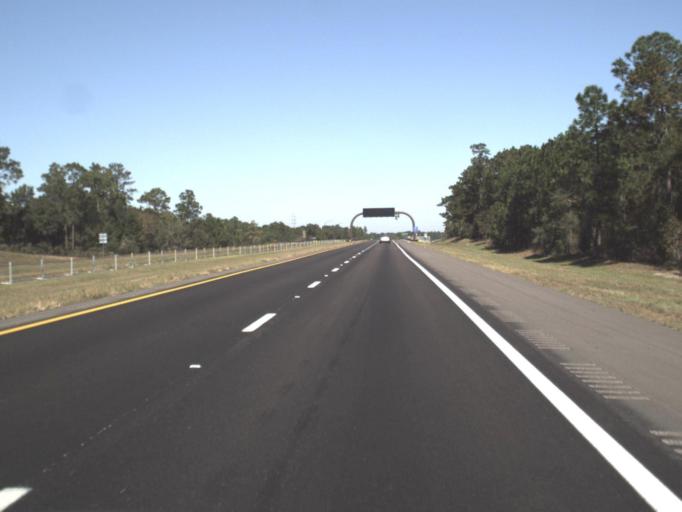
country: US
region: Florida
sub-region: Hernando County
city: Brookridge
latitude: 28.5202
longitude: -82.4779
